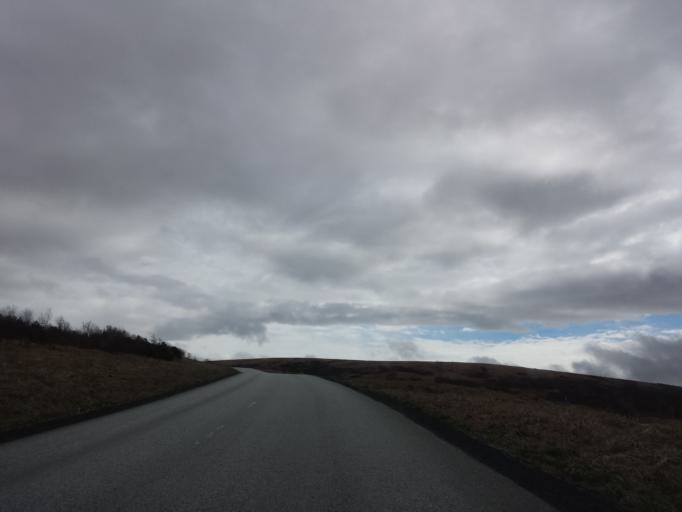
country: IS
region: Capital Region
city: Kopavogur
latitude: 64.0795
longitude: -21.8621
